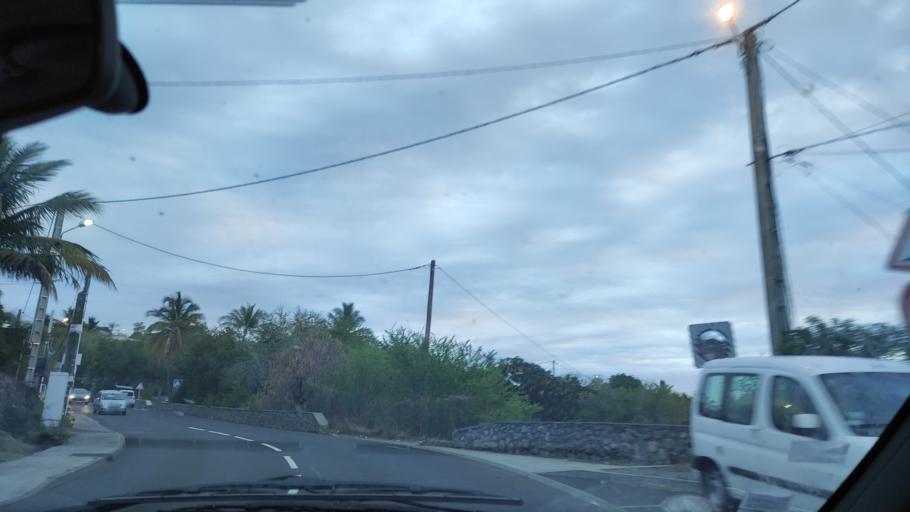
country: RE
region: Reunion
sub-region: Reunion
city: Saint-Leu
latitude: -21.1951
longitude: 55.2916
